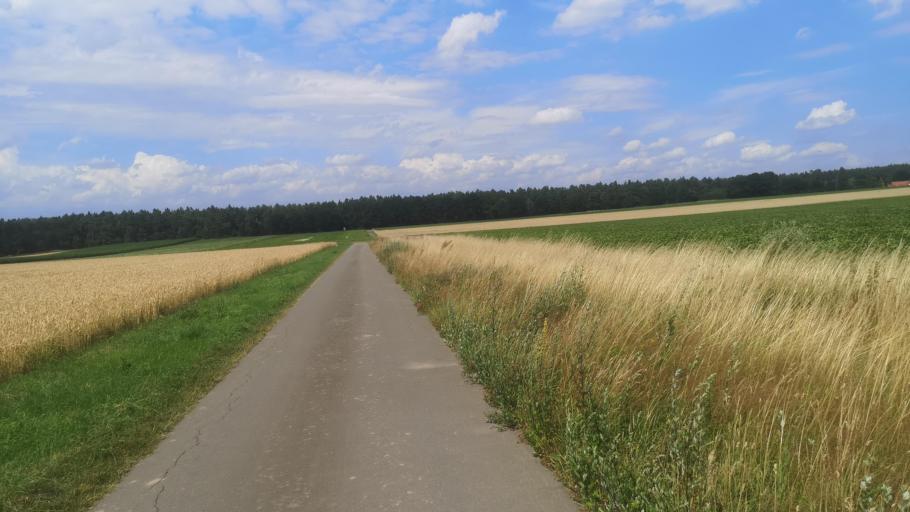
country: DE
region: Lower Saxony
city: Dahlem
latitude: 53.2305
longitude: 10.7461
